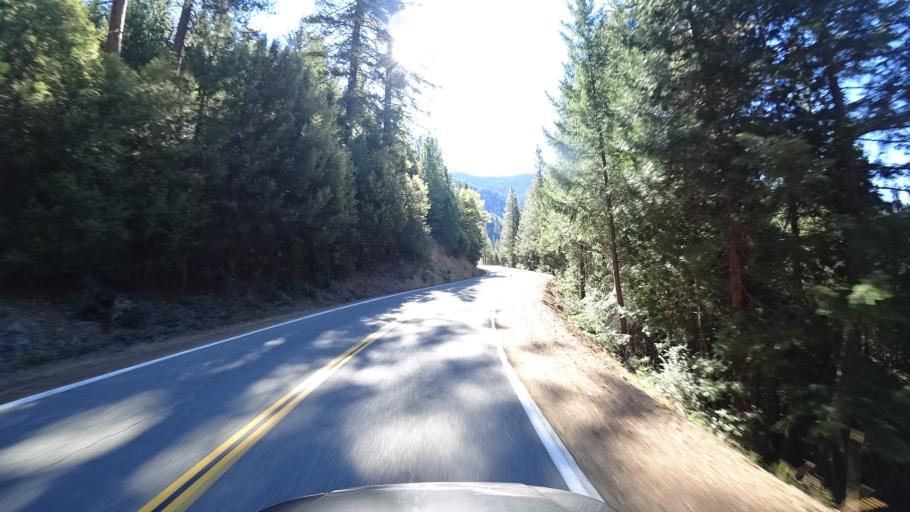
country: US
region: California
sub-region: Trinity County
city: Weaverville
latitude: 41.2249
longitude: -123.0153
